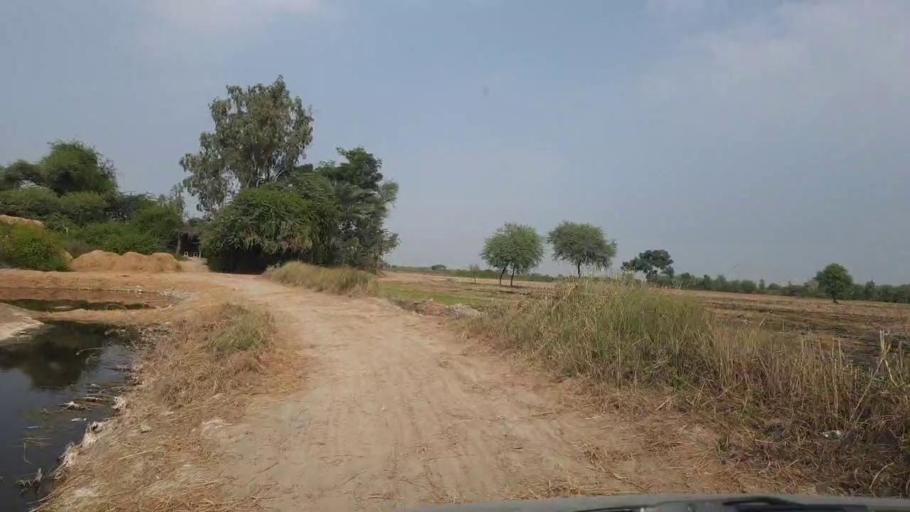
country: PK
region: Sindh
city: Matli
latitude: 24.9851
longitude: 68.7050
